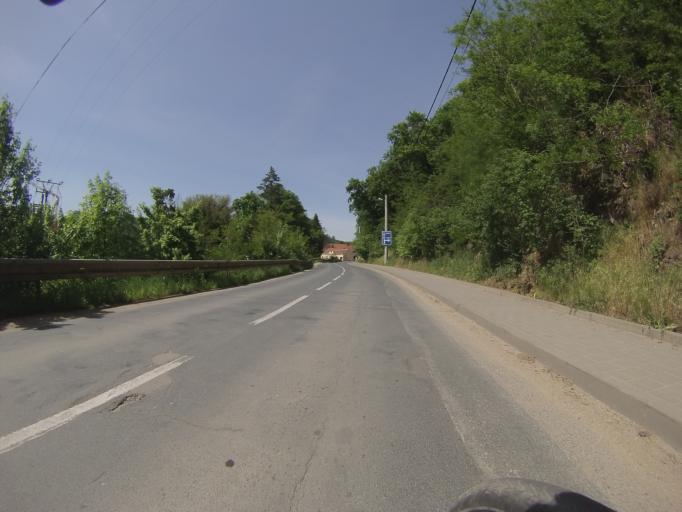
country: CZ
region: South Moravian
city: Bilovice nad Svitavou
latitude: 49.2464
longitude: 16.6748
